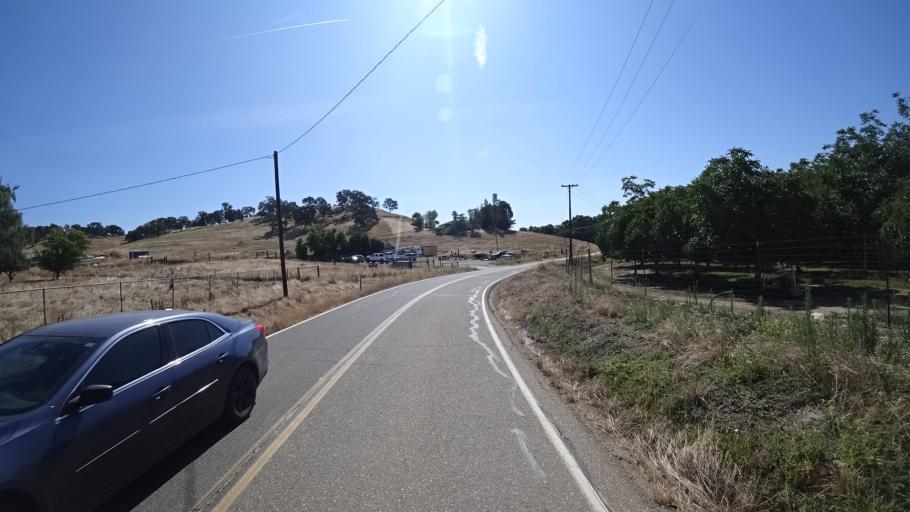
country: US
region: California
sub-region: Calaveras County
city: Rancho Calaveras
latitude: 38.0993
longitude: -120.8862
